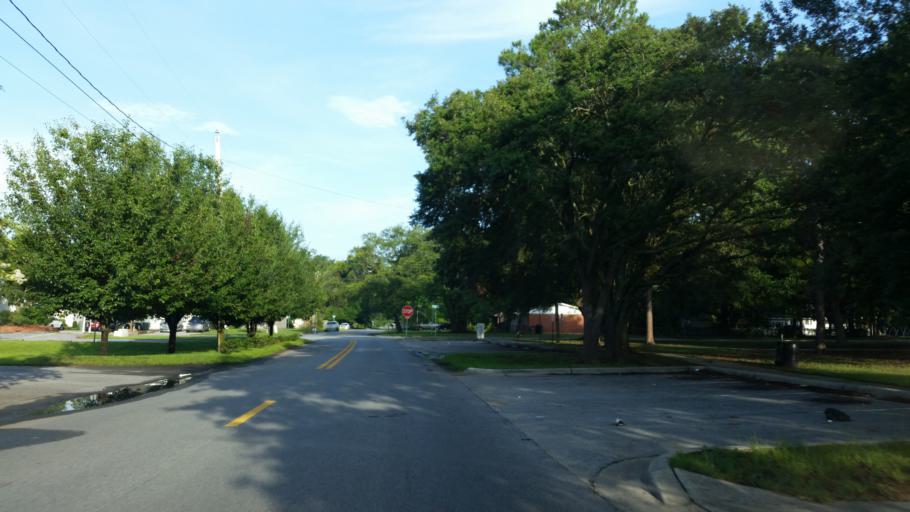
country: US
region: Florida
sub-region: Escambia County
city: Ferry Pass
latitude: 30.4917
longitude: -87.1950
